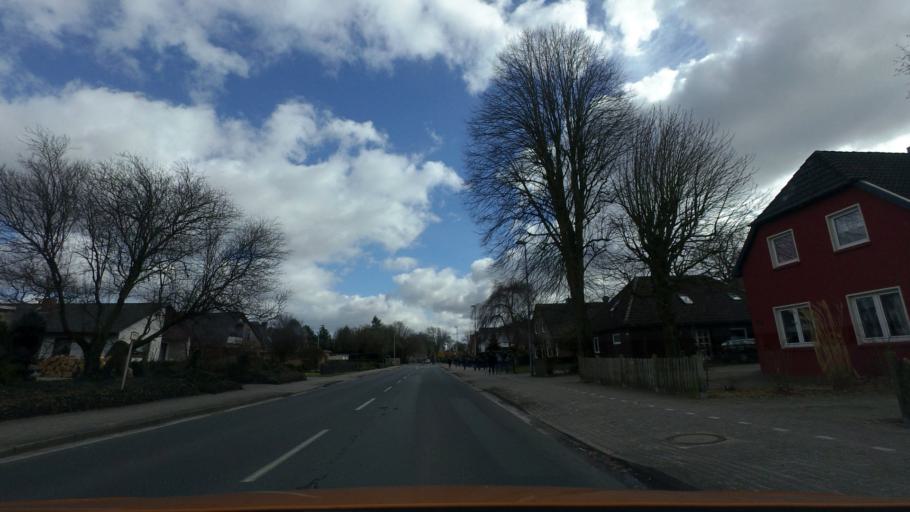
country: DE
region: Lower Saxony
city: Wiefelstede
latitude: 53.1408
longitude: 8.1044
